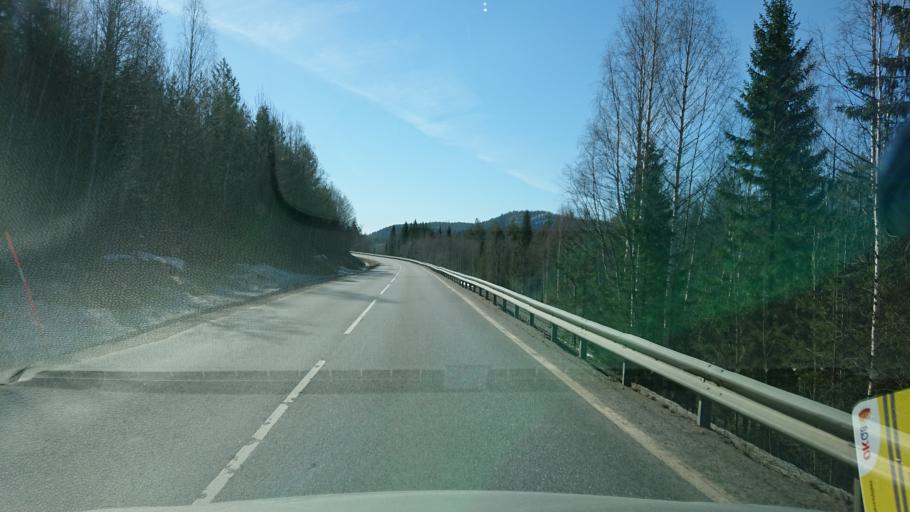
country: SE
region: Vaesterbotten
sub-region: Dorotea Kommun
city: Dorotea
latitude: 64.0439
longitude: 16.2582
